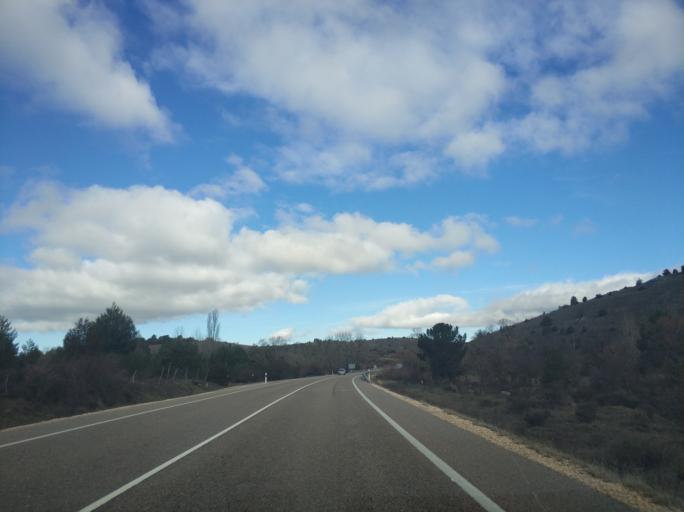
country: ES
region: Castille and Leon
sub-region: Provincia de Burgos
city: Rabanera del Pinar
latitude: 41.8790
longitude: -3.2243
